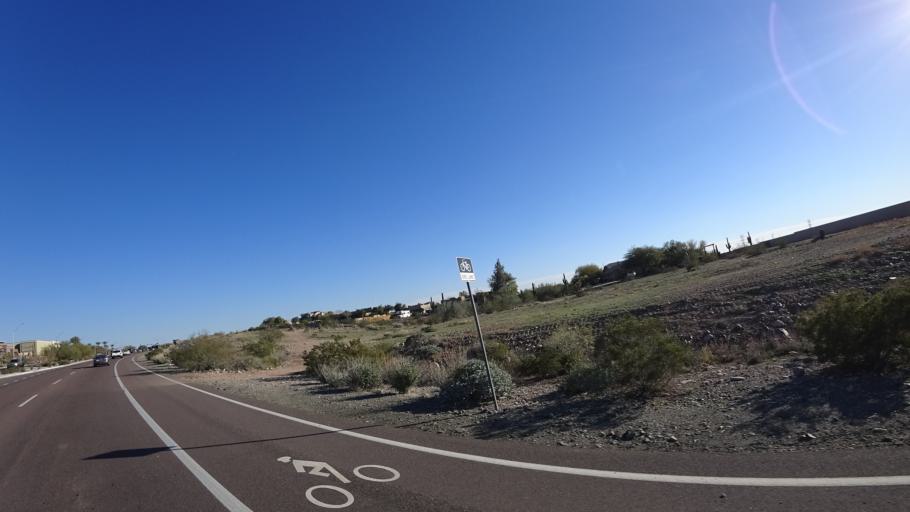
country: US
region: Arizona
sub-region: Maricopa County
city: Sun City West
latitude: 33.7134
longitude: -112.2809
